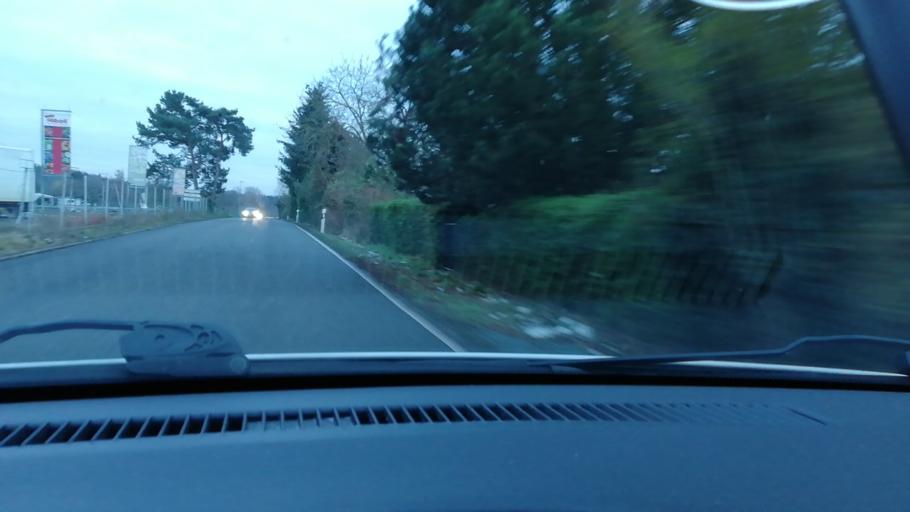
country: DE
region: Hesse
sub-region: Regierungsbezirk Darmstadt
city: Rodenbach
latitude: 50.1454
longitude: 9.0274
